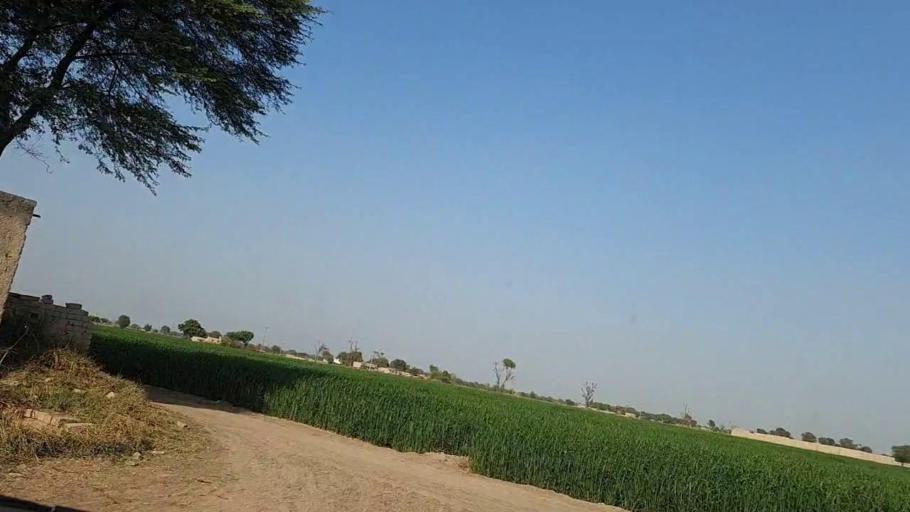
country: PK
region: Sindh
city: Sakrand
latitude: 26.1210
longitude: 68.2405
